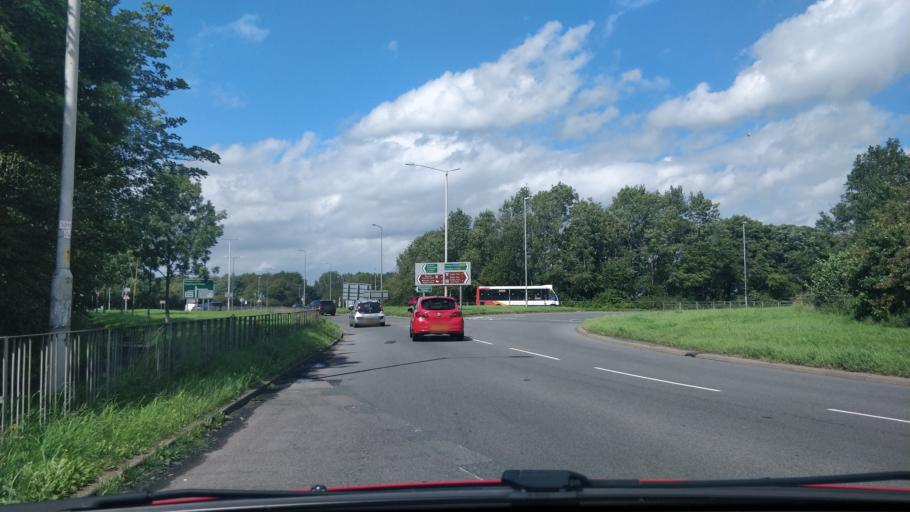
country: GB
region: England
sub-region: Borough of Wigan
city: Shevington
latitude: 53.5895
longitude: -2.6951
